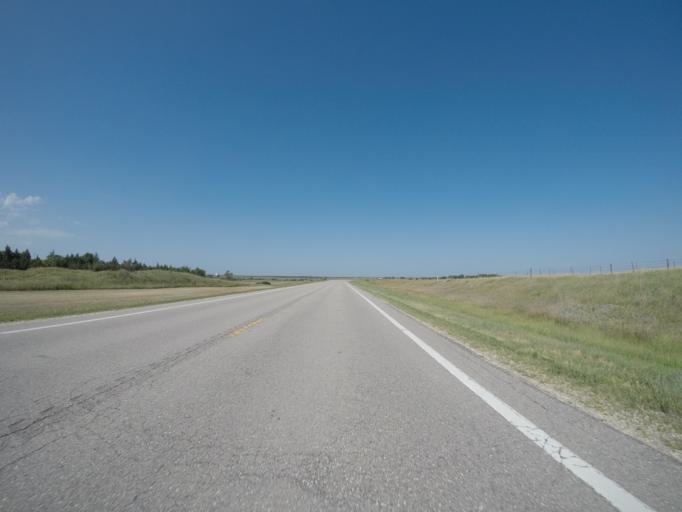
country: US
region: Kansas
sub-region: Clay County
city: Clay Center
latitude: 39.3658
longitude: -97.4191
